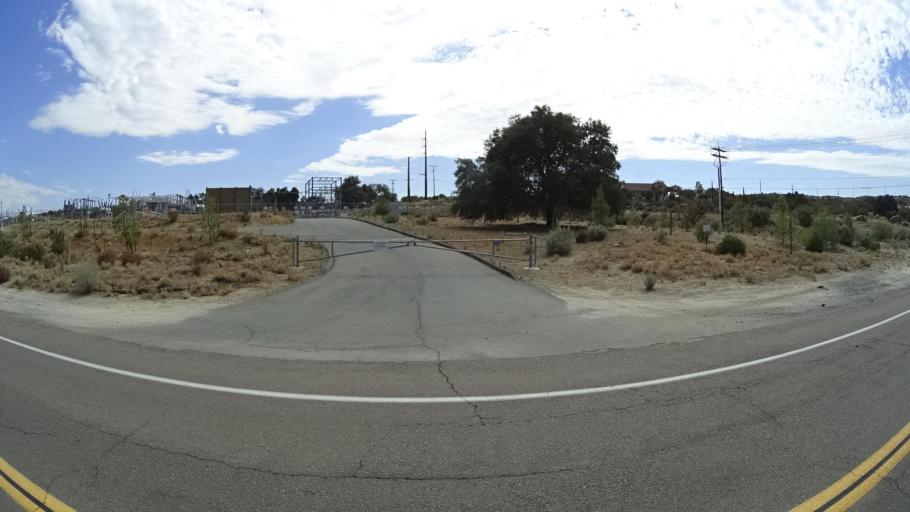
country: MX
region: Baja California
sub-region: Tecate
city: Cereso del Hongo
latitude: 32.6632
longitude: -116.2724
